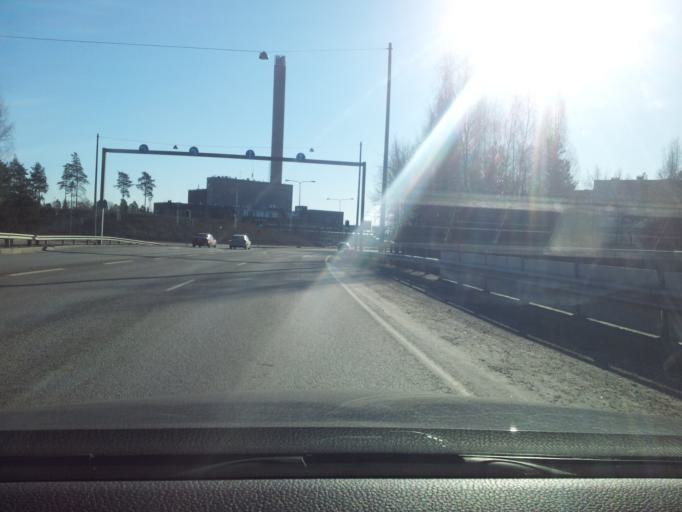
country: FI
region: Uusimaa
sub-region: Helsinki
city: Vantaa
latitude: 60.2273
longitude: 25.0741
